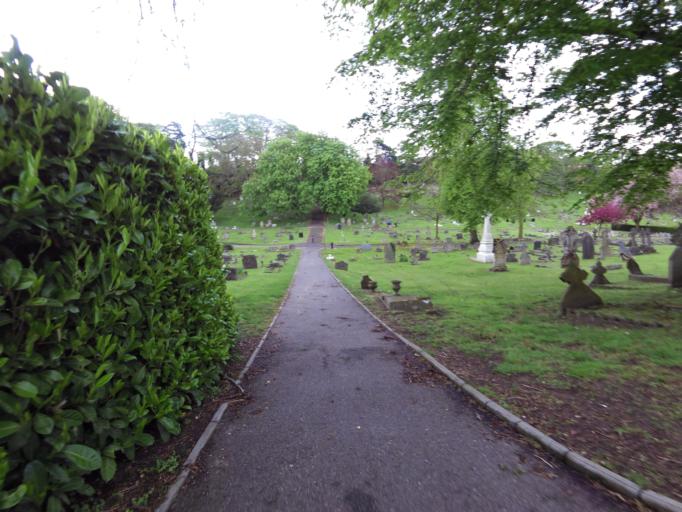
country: GB
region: England
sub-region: Suffolk
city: Ipswich
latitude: 52.0643
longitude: 1.1689
